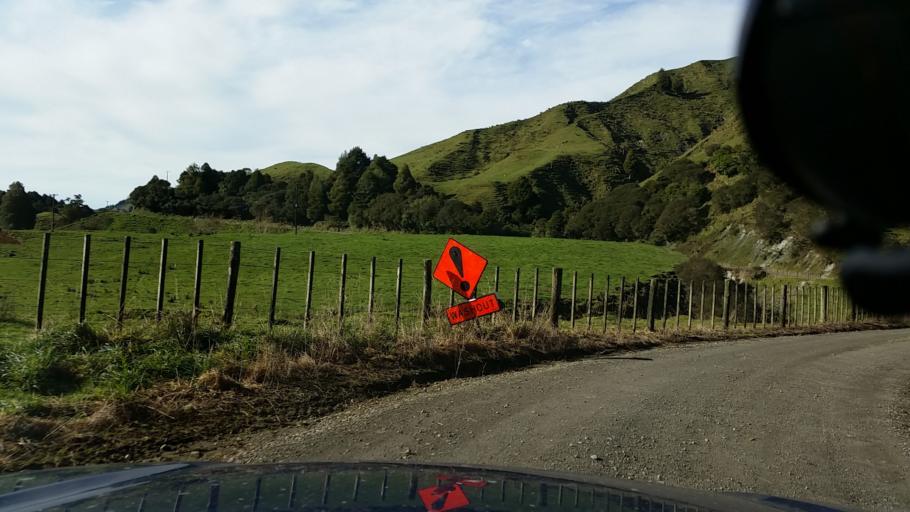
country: NZ
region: Taranaki
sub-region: New Plymouth District
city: Waitara
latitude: -39.0523
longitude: 174.7515
